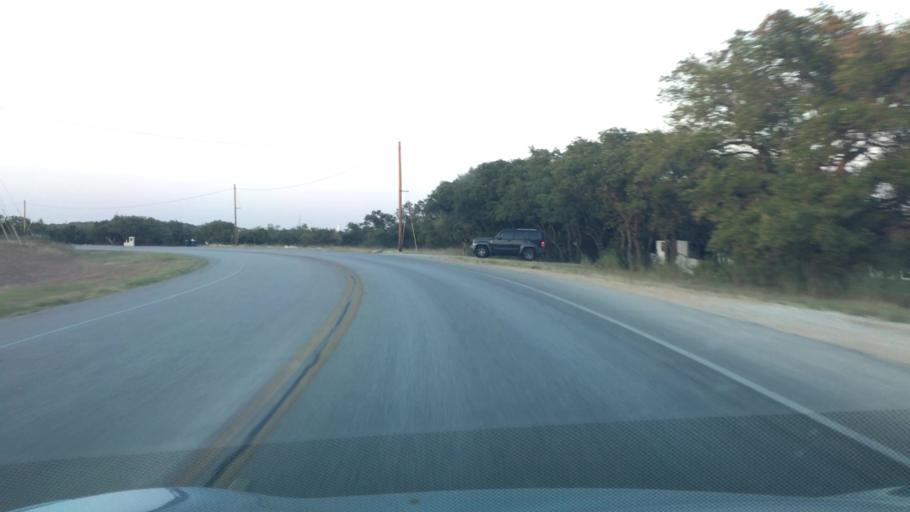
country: US
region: Texas
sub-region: Hays County
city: Dripping Springs
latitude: 30.1914
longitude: -97.9981
